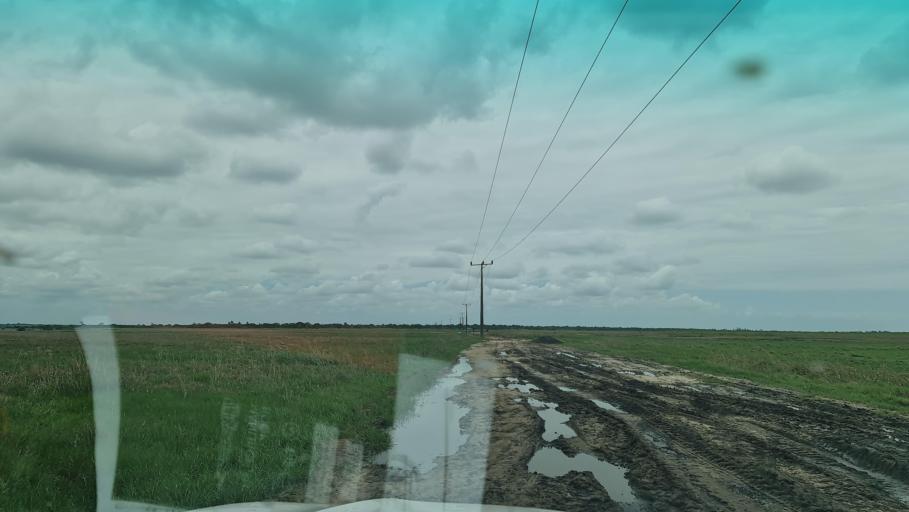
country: MZ
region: Maputo City
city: Maputo
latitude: -25.7148
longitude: 32.7022
